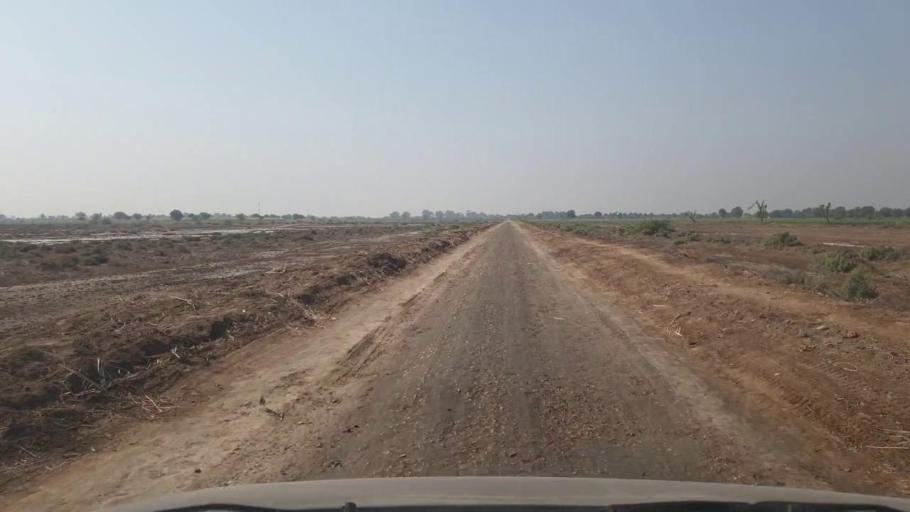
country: PK
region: Sindh
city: Mirwah Gorchani
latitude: 25.2406
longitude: 69.0967
